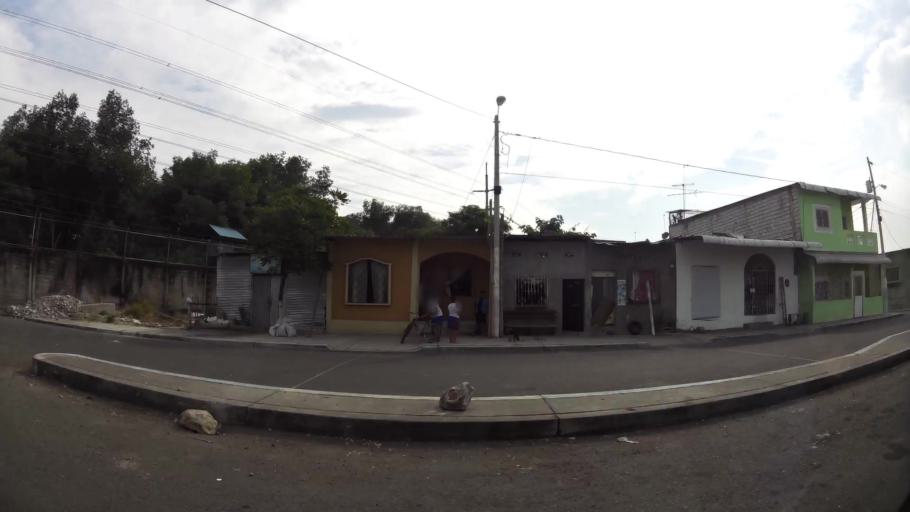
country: EC
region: Guayas
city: Guayaquil
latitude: -2.2610
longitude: -79.9033
